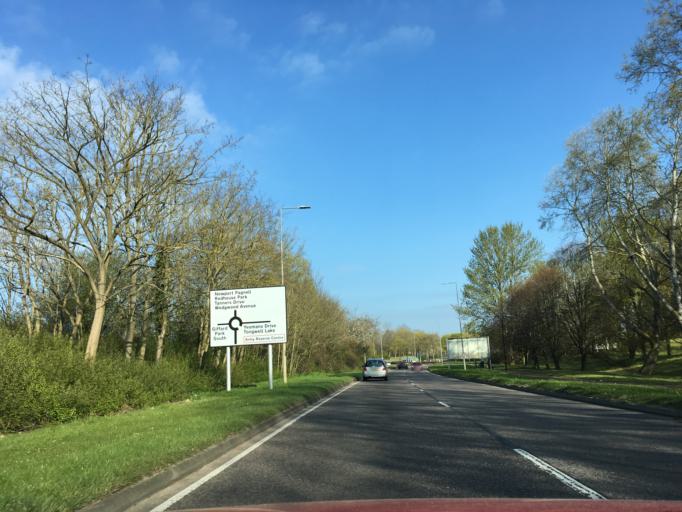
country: GB
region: England
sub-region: Milton Keynes
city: Newport Pagnell
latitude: 52.0674
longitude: -0.7402
